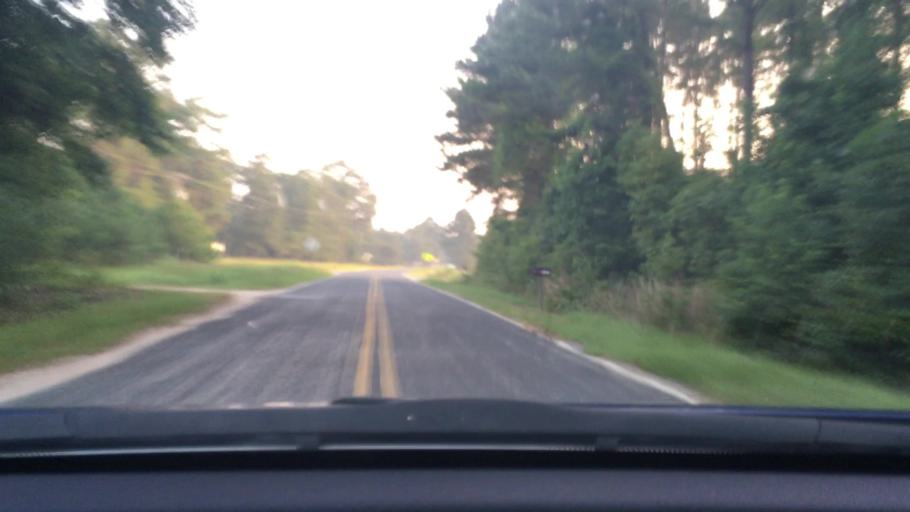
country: US
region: South Carolina
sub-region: Lee County
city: Bishopville
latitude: 34.2294
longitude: -80.1330
